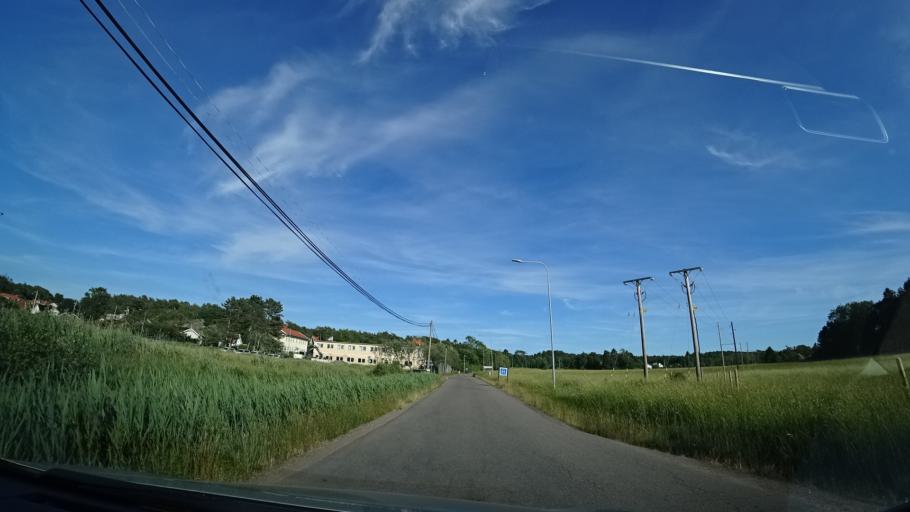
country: SE
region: Vaestra Goetaland
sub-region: Goteborg
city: Billdal
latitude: 57.5798
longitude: 11.9578
